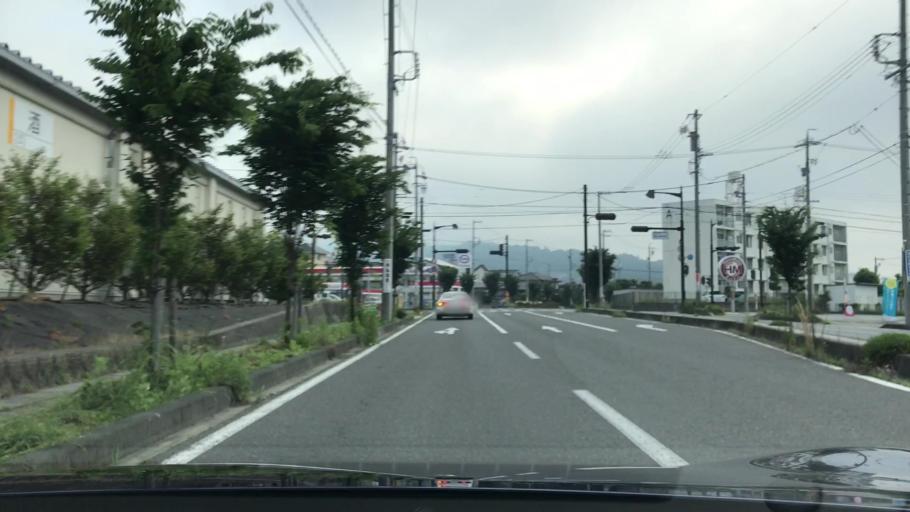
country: JP
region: Nagano
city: Iida
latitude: 35.5167
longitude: 137.8081
